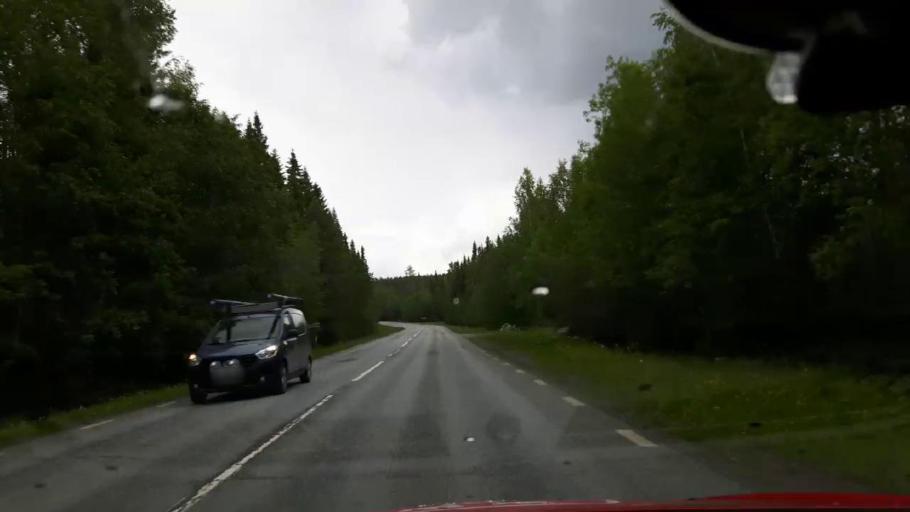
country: SE
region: Jaemtland
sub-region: Krokoms Kommun
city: Krokom
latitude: 63.4308
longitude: 14.2088
